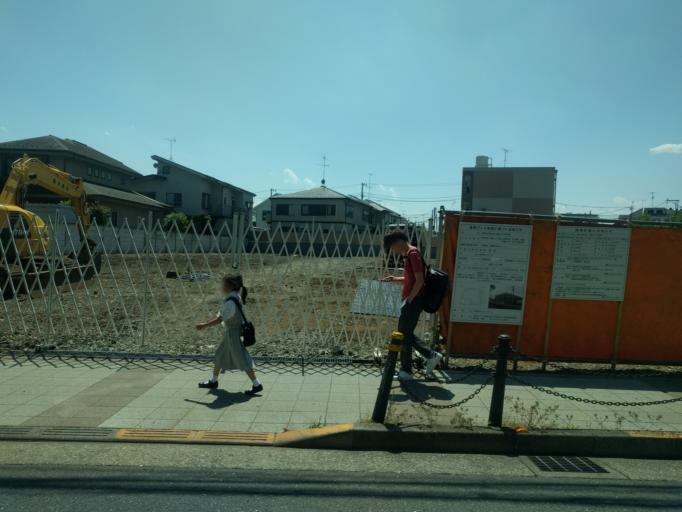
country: JP
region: Tokyo
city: Mitaka-shi
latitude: 35.6657
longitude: 139.6188
